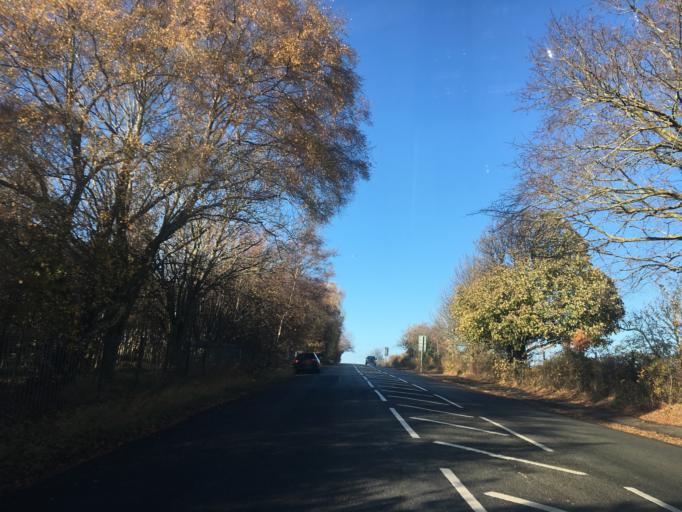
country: GB
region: Scotland
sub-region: Midlothian
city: Loanhead
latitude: 55.9140
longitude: -3.1789
